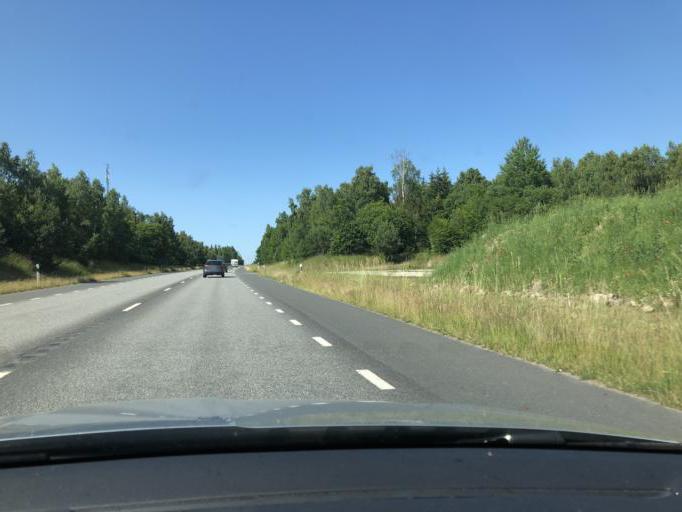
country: SE
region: Skane
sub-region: Bromolla Kommun
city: Bromoella
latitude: 56.0692
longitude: 14.4988
